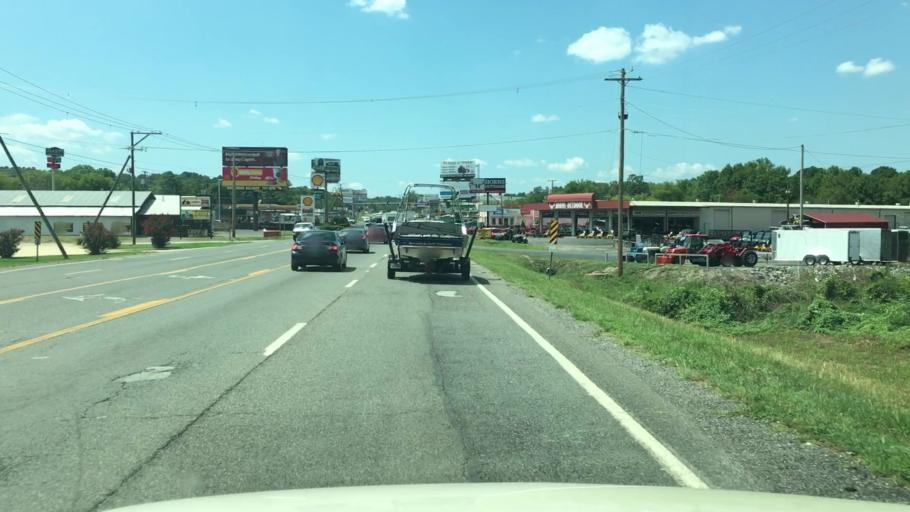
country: US
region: Arkansas
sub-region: Garland County
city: Piney
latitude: 34.5015
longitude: -93.1235
